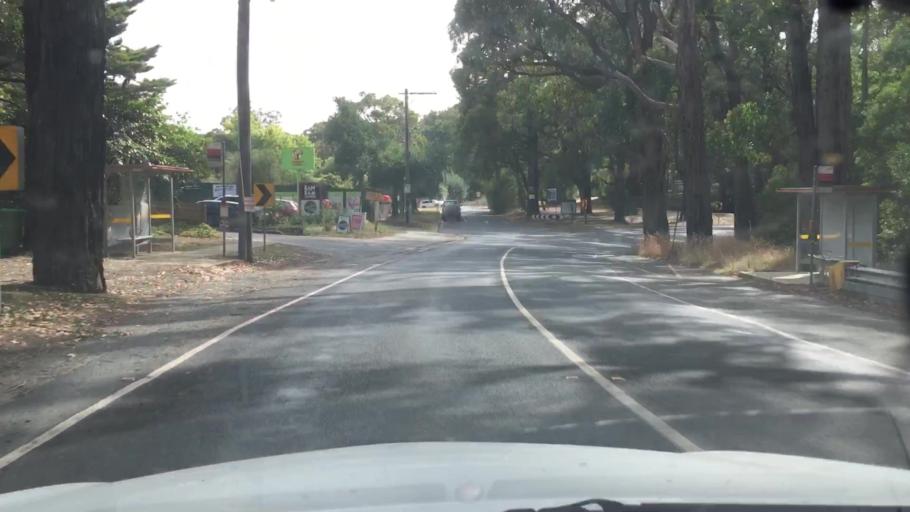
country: AU
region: Victoria
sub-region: Cardinia
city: Emerald
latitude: -37.9215
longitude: 145.4659
